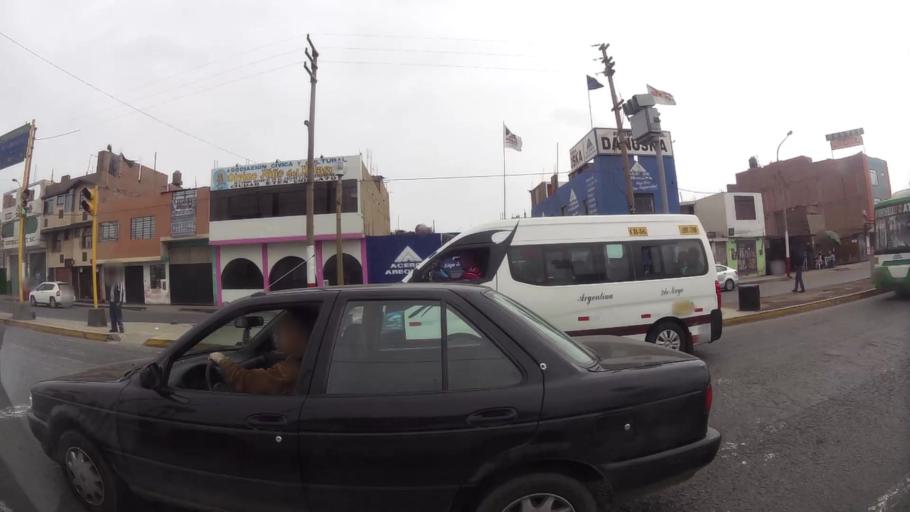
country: PE
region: Callao
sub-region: Callao
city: Callao
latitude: -12.0012
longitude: -77.1173
